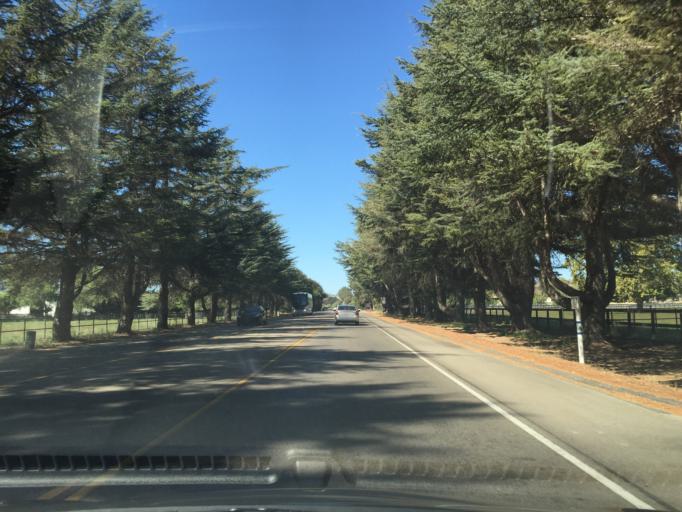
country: US
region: California
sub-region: Santa Barbara County
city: Buellton
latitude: 34.6049
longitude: -120.1725
